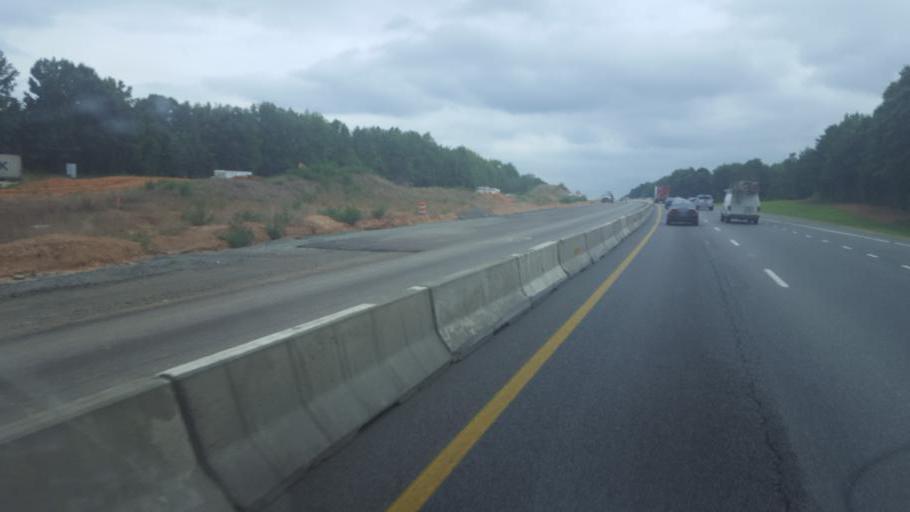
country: US
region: North Carolina
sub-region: Mecklenburg County
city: Cornelius
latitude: 35.4491
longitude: -80.8693
